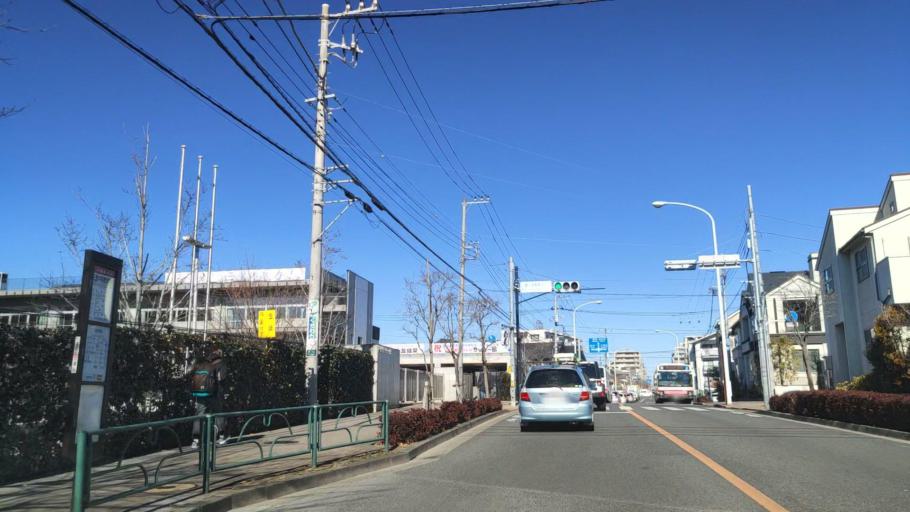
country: JP
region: Tokyo
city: Mitaka-shi
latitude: 35.6793
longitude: 139.5678
